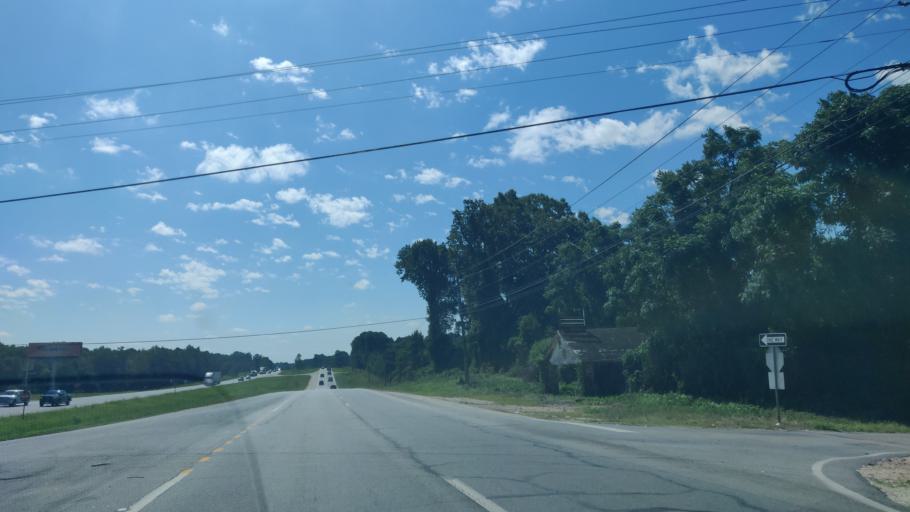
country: US
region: Alabama
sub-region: Lee County
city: Smiths Station
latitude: 32.5827
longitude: -85.1648
